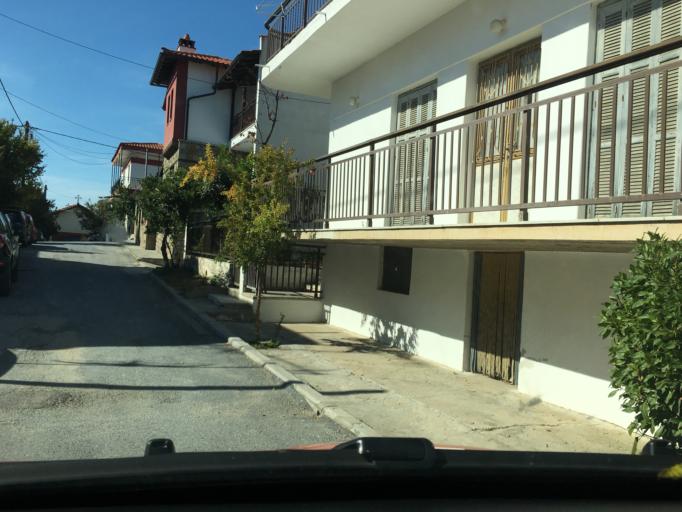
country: GR
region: Central Macedonia
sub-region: Nomos Chalkidikis
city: Ouranoupolis
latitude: 40.3253
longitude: 23.9827
